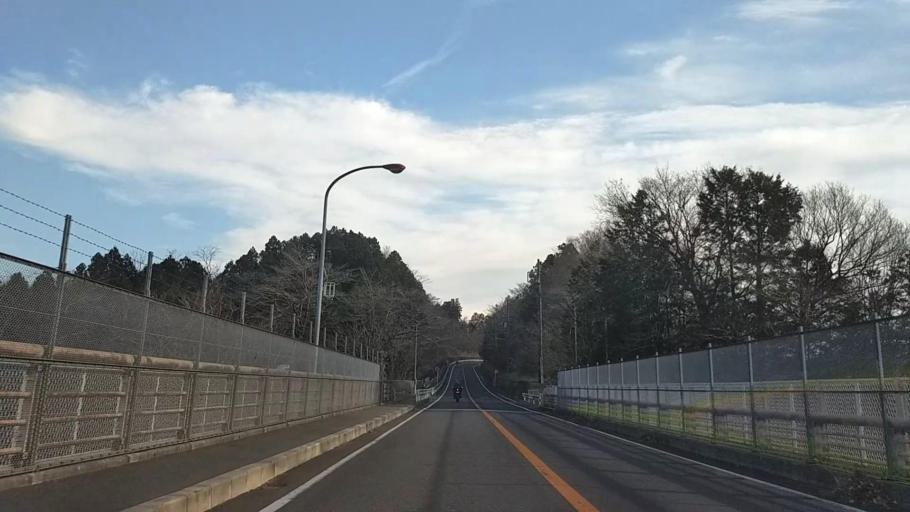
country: JP
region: Yamanashi
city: Uenohara
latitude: 35.5324
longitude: 139.2191
